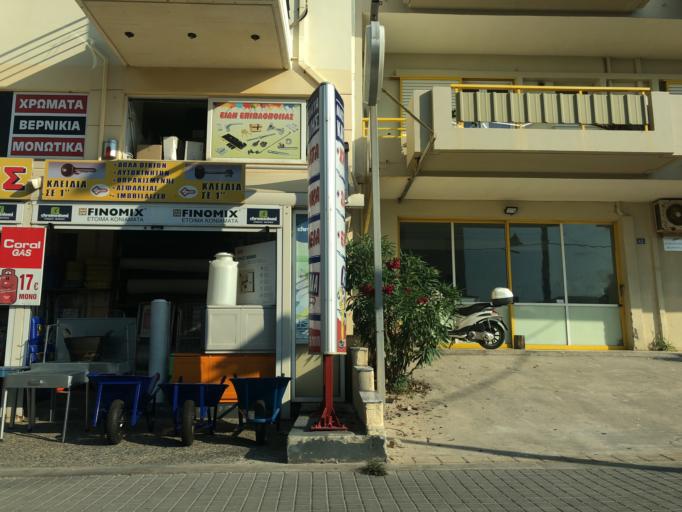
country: GR
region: Crete
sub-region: Nomos Rethymnis
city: Rethymno
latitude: 35.3655
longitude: 24.4655
